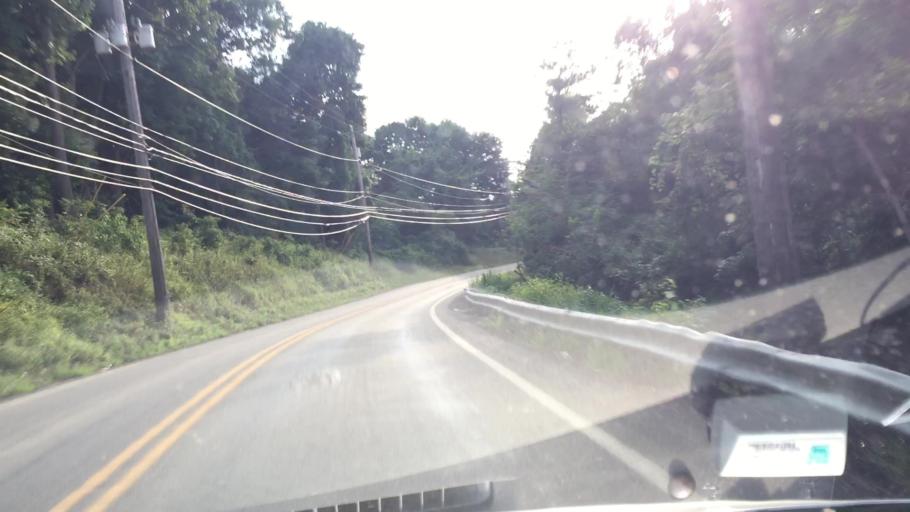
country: US
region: Pennsylvania
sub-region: Allegheny County
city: Carnot-Moon
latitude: 40.5110
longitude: -80.2467
